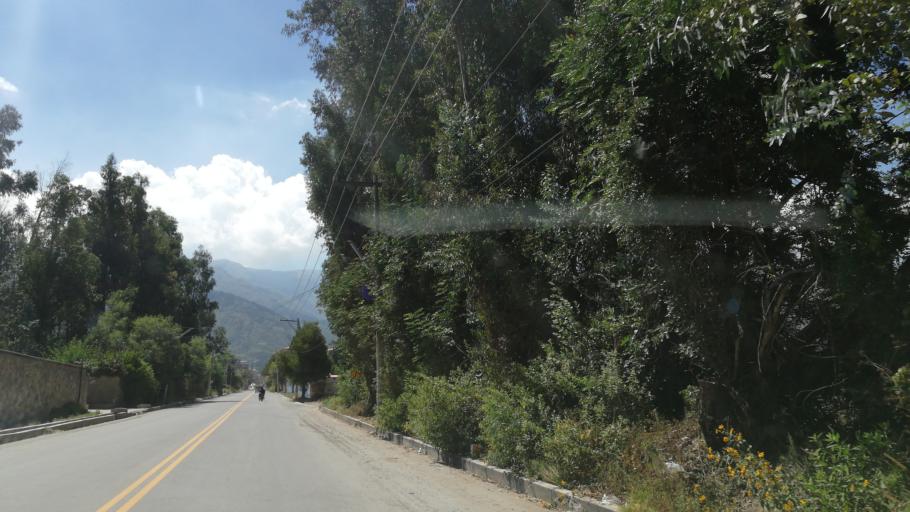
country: BO
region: Cochabamba
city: Cochabamba
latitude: -17.3439
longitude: -66.2231
